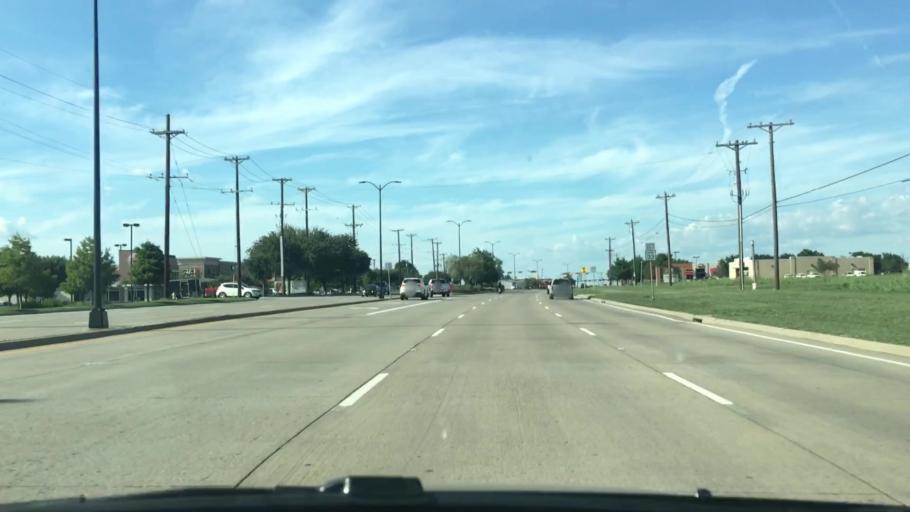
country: US
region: Texas
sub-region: Collin County
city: Frisco
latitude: 33.1468
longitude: -96.8045
